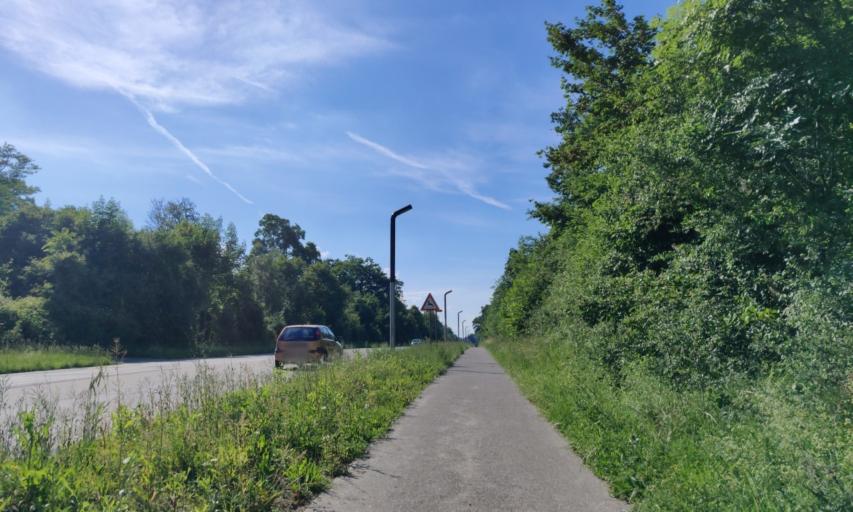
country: CH
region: Basel-Landschaft
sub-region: Bezirk Arlesheim
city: Muttenz
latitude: 47.5388
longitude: 7.6572
